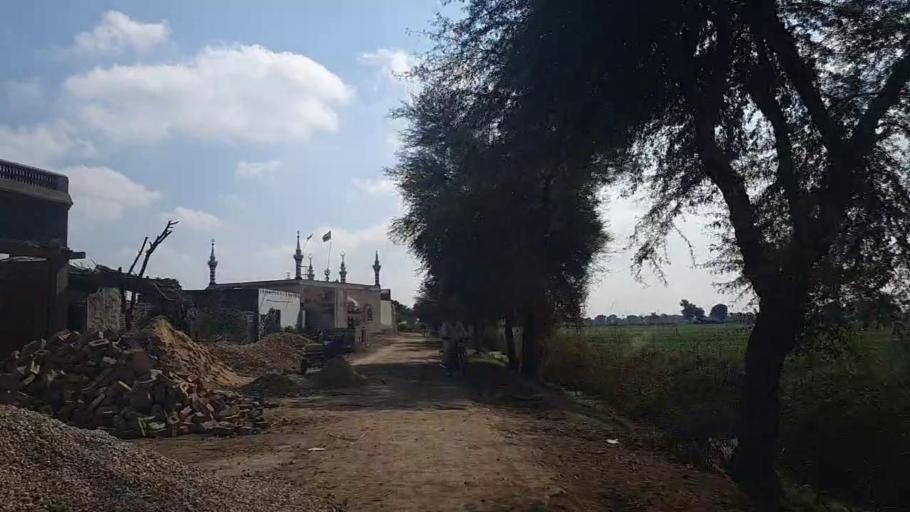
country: PK
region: Sindh
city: Sanghar
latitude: 26.0470
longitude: 68.9786
